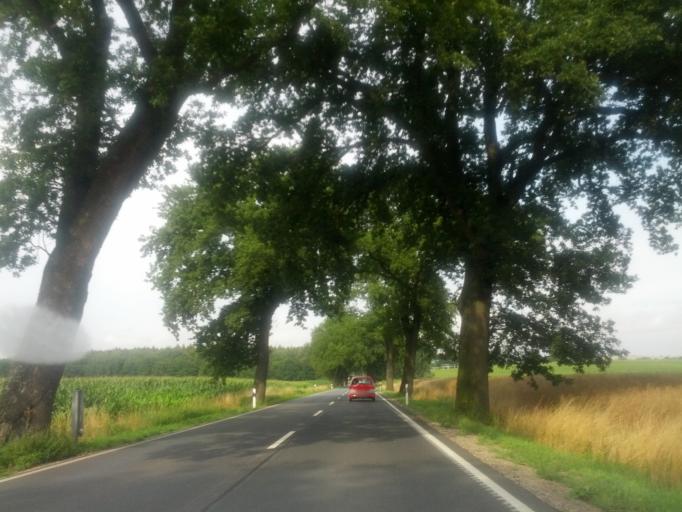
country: DE
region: Mecklenburg-Vorpommern
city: Sellin
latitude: 53.9175
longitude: 11.5875
